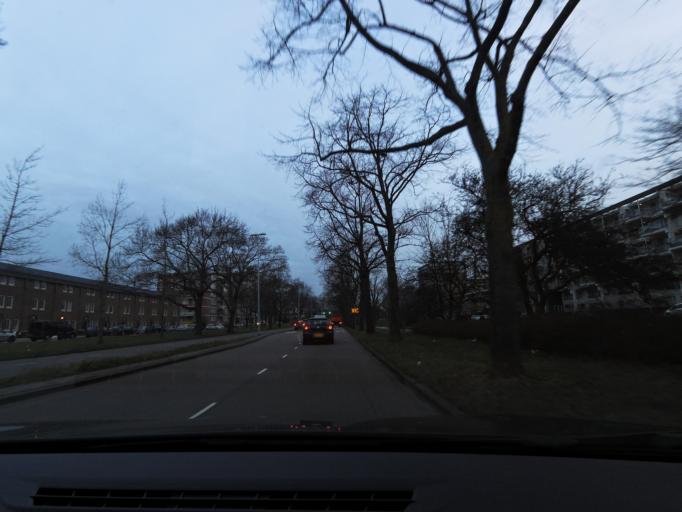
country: NL
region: South Holland
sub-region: Gemeente Rijswijk
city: Rijswijk
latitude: 52.0490
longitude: 4.3016
